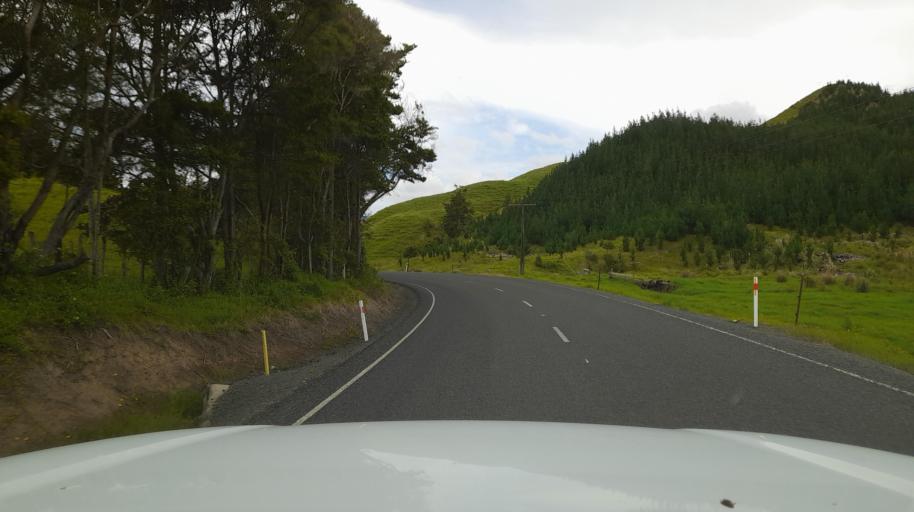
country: NZ
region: Northland
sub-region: Far North District
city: Kaitaia
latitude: -35.2996
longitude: 173.3633
